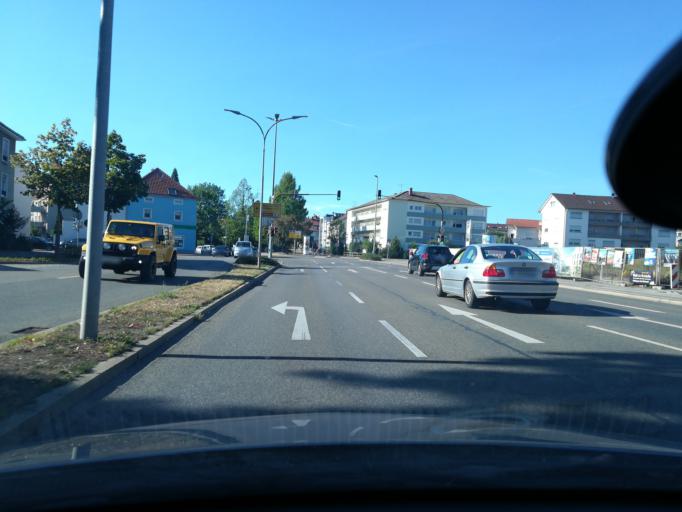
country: DE
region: Baden-Wuerttemberg
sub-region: Freiburg Region
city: Singen
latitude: 47.7627
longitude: 8.8342
